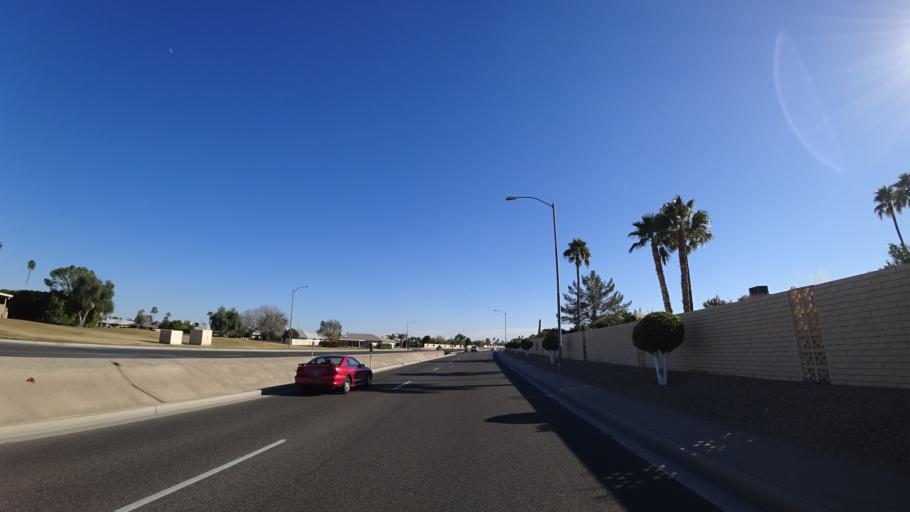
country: US
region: Arizona
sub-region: Maricopa County
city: Sun City West
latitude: 33.6710
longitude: -112.3339
